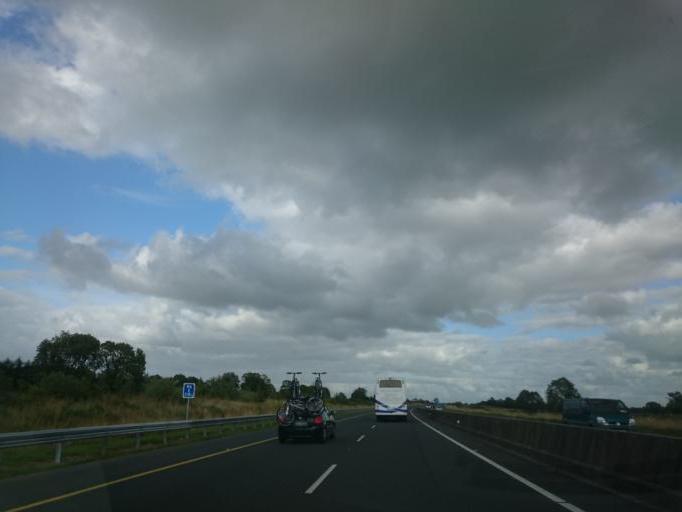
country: IE
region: Connaught
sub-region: County Galway
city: Athenry
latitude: 53.2699
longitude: -8.6577
